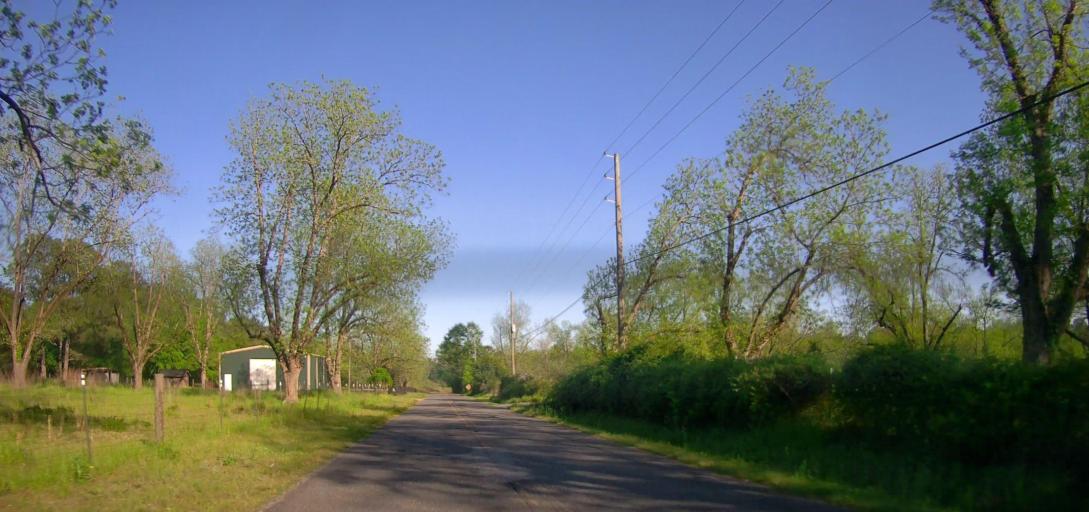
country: US
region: Georgia
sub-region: Houston County
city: Perry
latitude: 32.4814
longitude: -83.7997
